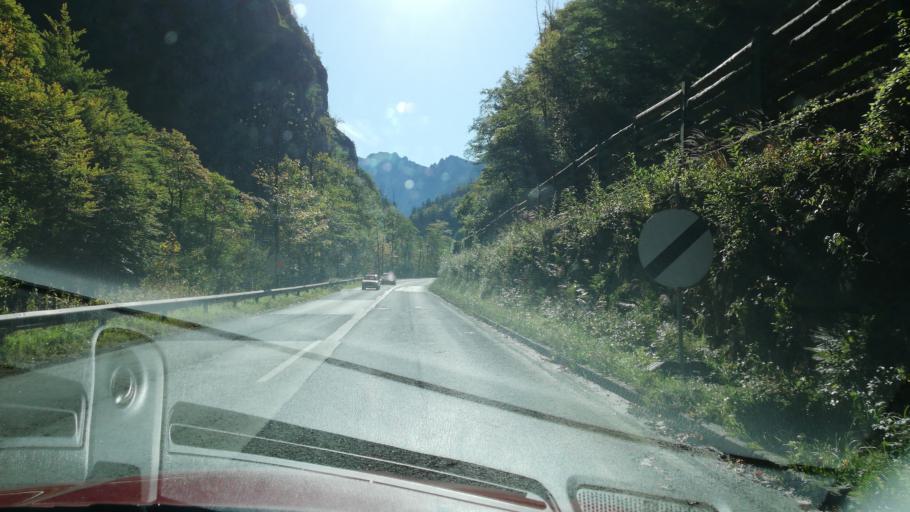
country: AT
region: Styria
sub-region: Politischer Bezirk Leoben
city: Hieflau
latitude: 47.5929
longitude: 14.7516
